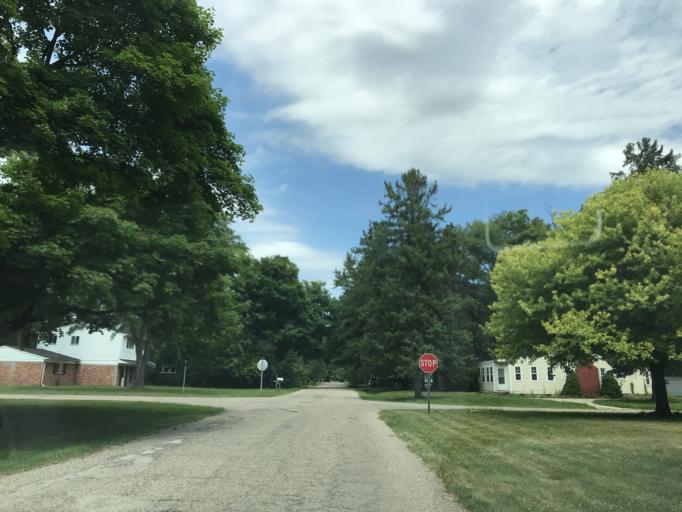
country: US
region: Michigan
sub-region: Oakland County
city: Bingham Farms
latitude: 42.4752
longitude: -83.2640
